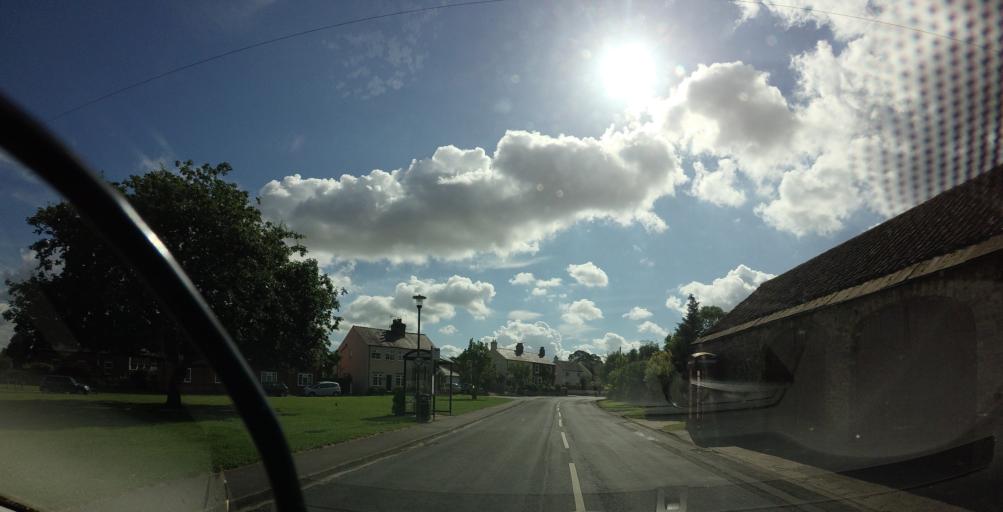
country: GB
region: England
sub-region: North Yorkshire
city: Boroughbridge
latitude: 54.0592
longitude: -1.4419
